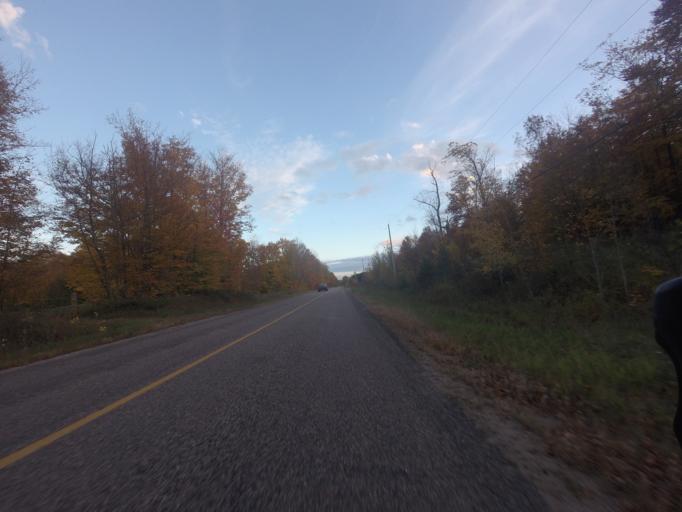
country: CA
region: Ontario
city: Renfrew
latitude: 45.4280
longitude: -76.9576
